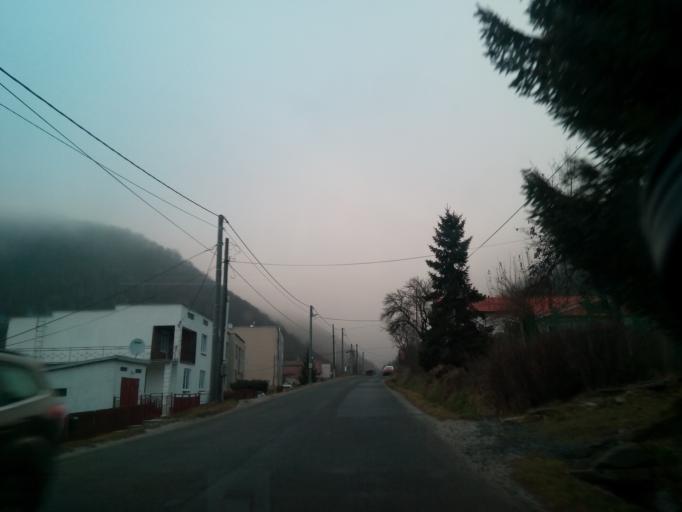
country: SK
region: Kosicky
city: Krompachy
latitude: 48.9378
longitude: 20.9416
